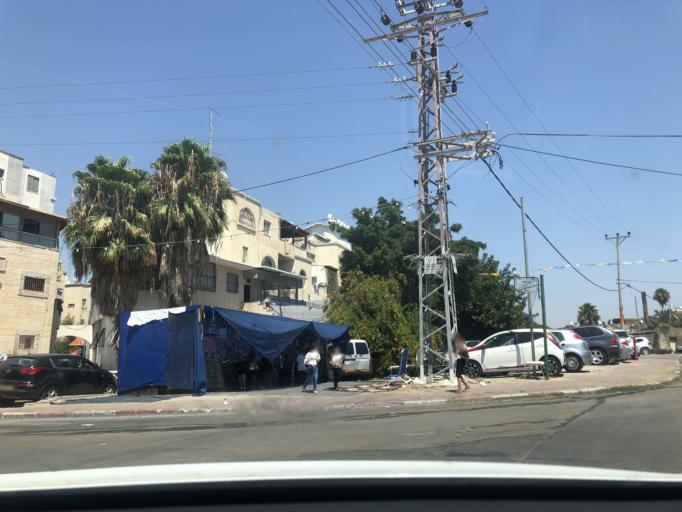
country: IL
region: Central District
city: Lod
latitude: 31.9568
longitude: 34.9020
